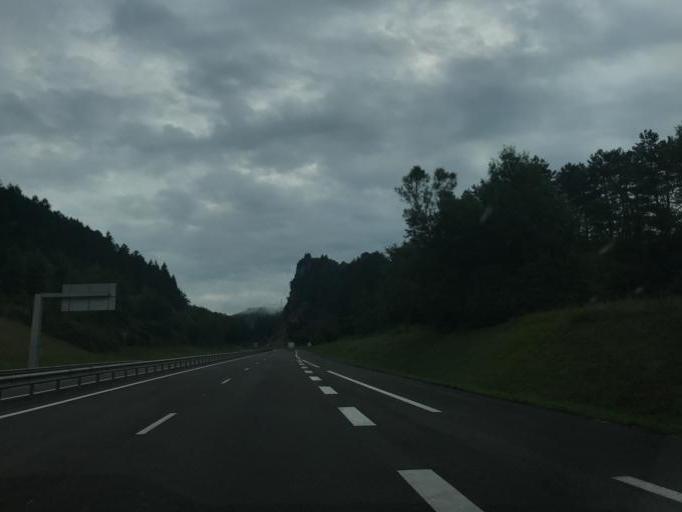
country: FR
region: Rhone-Alpes
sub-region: Departement de l'Ain
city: Montreal-la-Cluse
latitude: 46.1811
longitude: 5.5622
